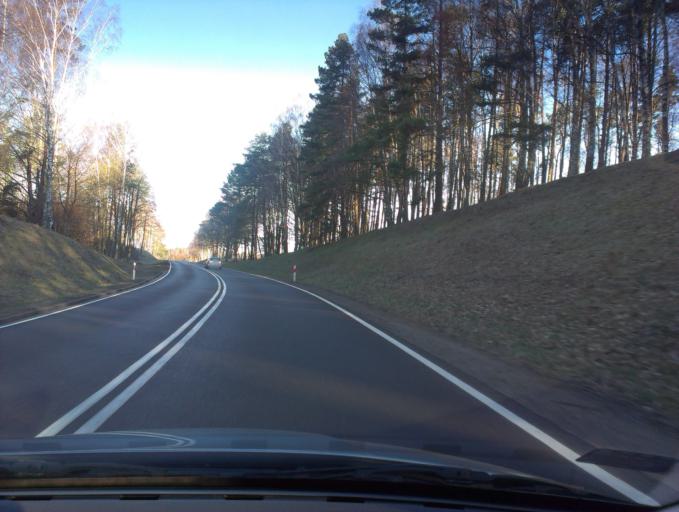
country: PL
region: West Pomeranian Voivodeship
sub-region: Powiat koszalinski
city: Bobolice
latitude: 54.0113
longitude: 16.5045
